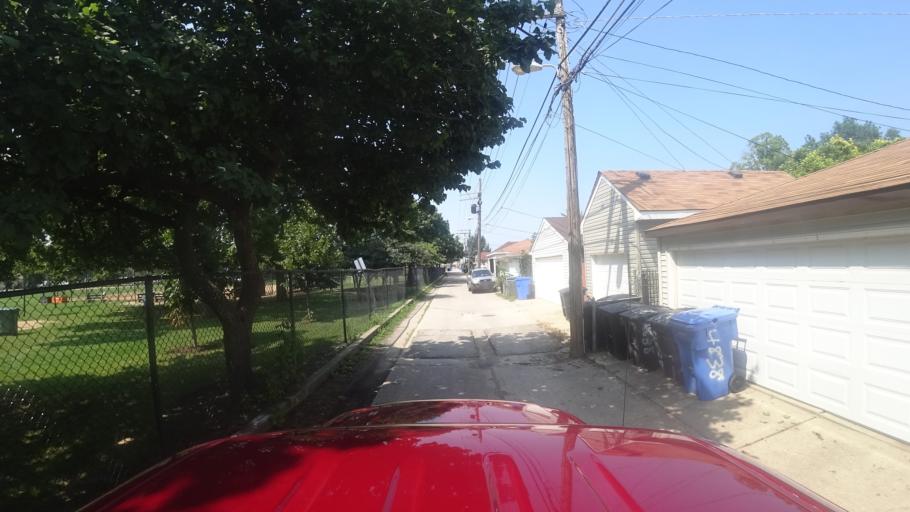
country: US
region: Illinois
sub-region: Cook County
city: Cicero
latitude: 41.8047
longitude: -87.7340
